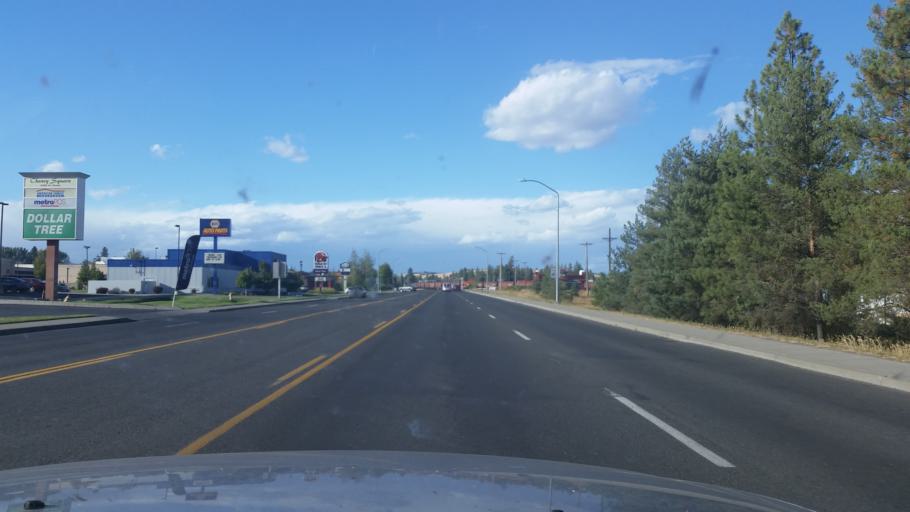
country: US
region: Washington
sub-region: Spokane County
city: Cheney
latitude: 47.5024
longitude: -117.5646
